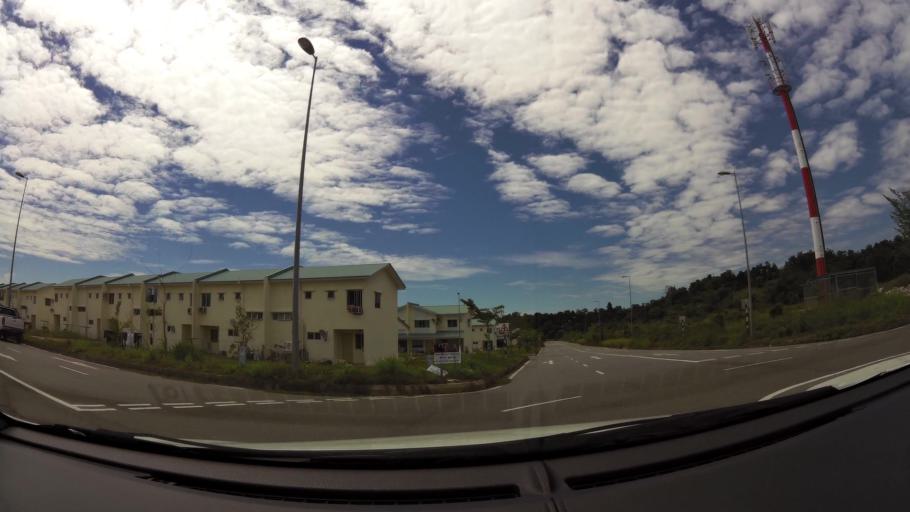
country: BN
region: Brunei and Muara
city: Bandar Seri Begawan
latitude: 4.9726
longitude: 115.0115
